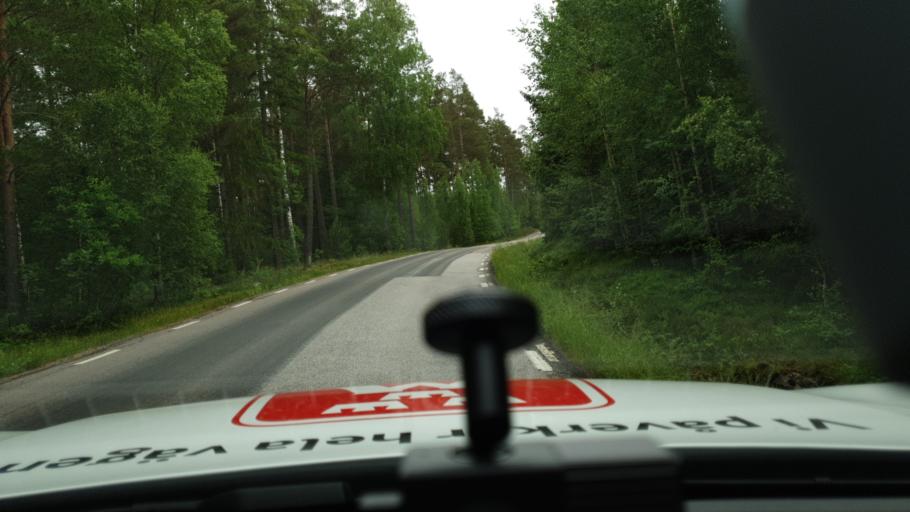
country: SE
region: Vaestra Goetaland
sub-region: Skovde Kommun
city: Stopen
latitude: 58.5660
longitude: 13.8560
